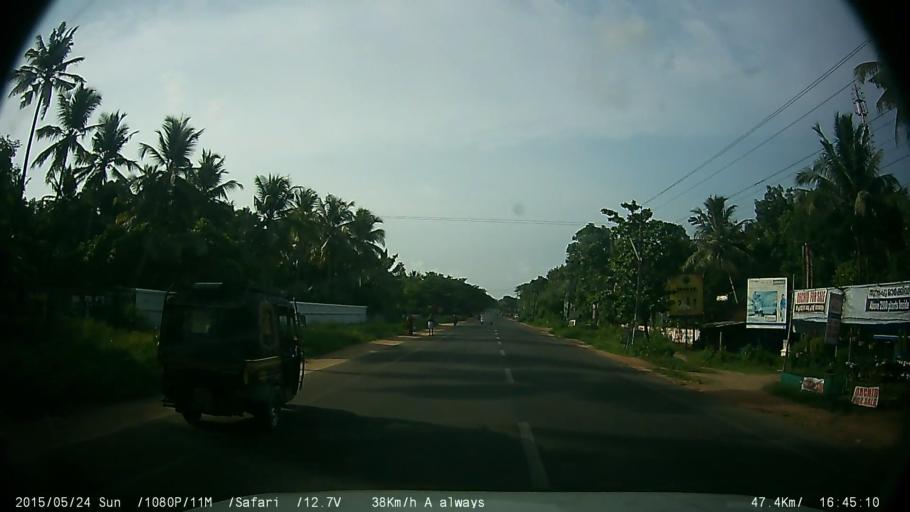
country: IN
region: Kerala
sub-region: Alappuzha
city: Shertallai
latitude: 9.6590
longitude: 76.3379
